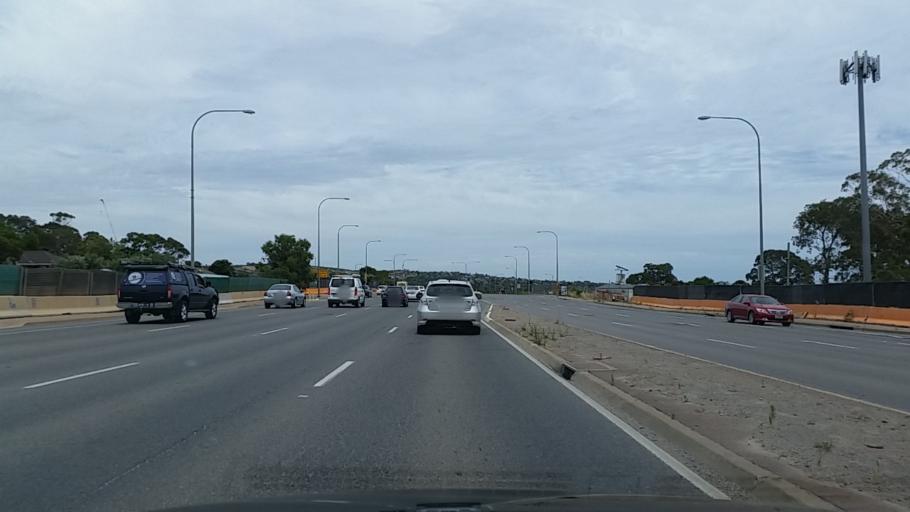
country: AU
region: South Australia
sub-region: Marion
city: Marion
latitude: -35.0146
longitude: 138.5722
